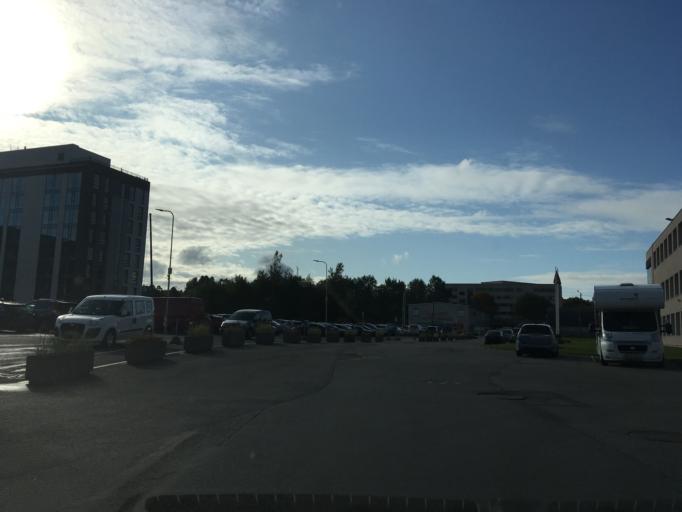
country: EE
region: Harju
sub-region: Saue vald
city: Laagri
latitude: 59.3972
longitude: 24.6571
